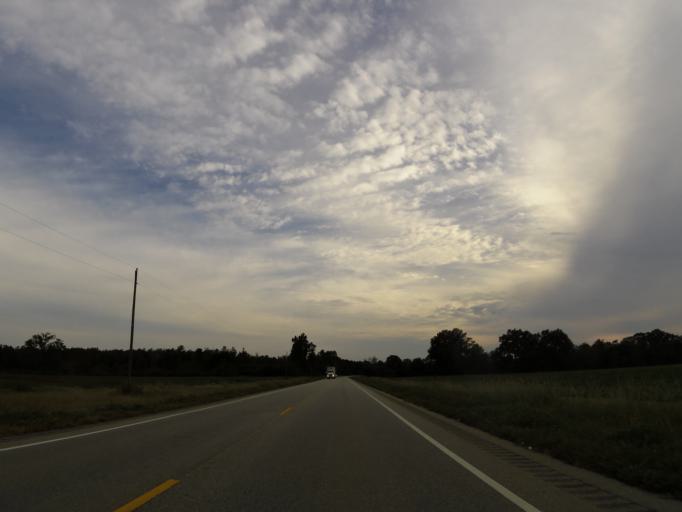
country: US
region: Alabama
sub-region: Monroe County
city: Frisco City
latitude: 31.3668
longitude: -87.4323
